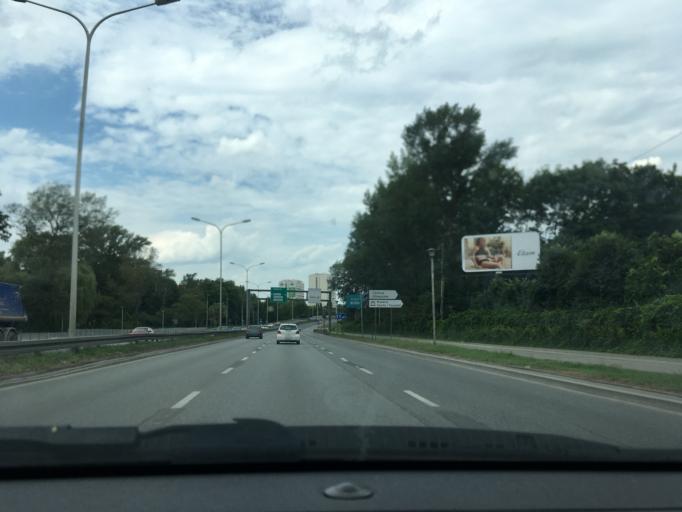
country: PL
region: Masovian Voivodeship
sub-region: Warszawa
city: Zoliborz
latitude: 52.2685
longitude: 21.0006
